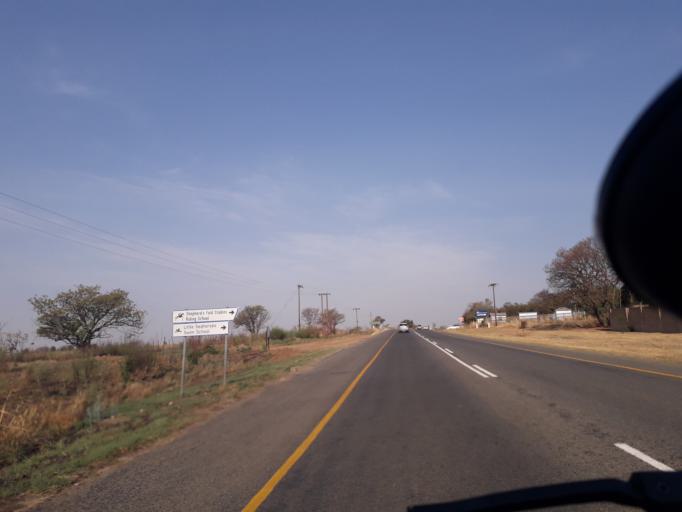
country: ZA
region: Gauteng
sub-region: West Rand District Municipality
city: Muldersdriseloop
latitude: -25.9631
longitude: 27.8955
